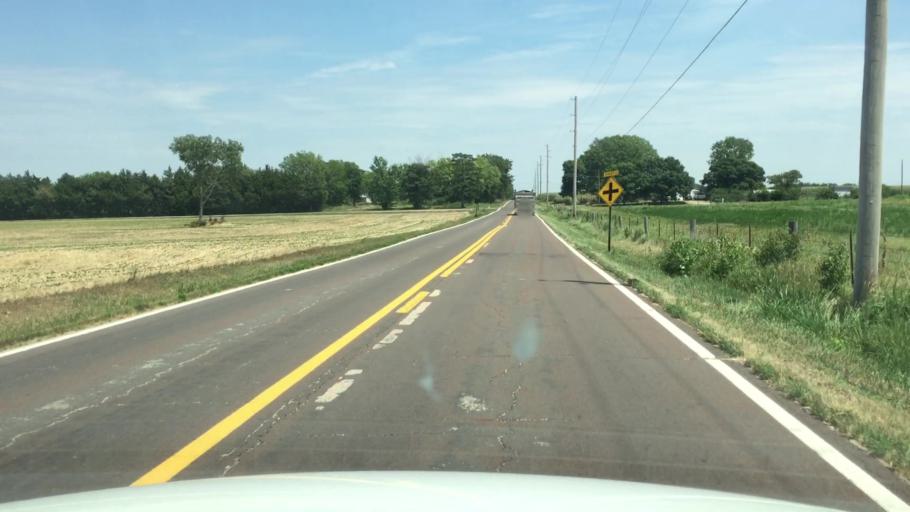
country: US
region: Kansas
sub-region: Shawnee County
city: Topeka
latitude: 38.9861
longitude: -95.5404
